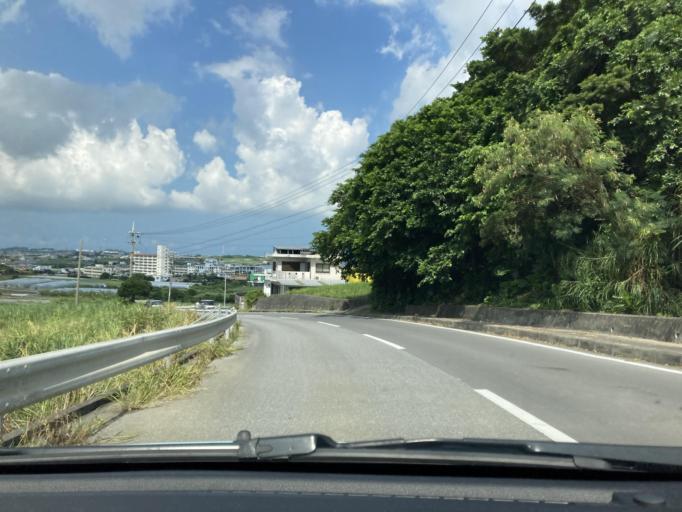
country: JP
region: Okinawa
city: Tomigusuku
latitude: 26.1497
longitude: 127.7580
